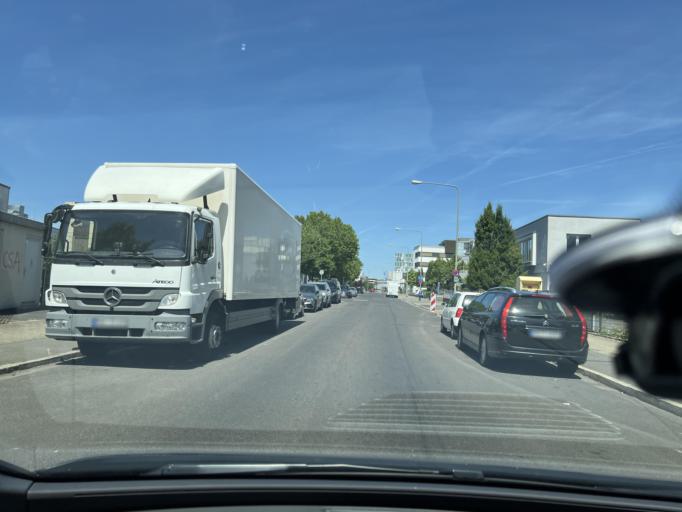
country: DE
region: Hesse
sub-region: Regierungsbezirk Darmstadt
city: Offenbach
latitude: 50.1202
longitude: 8.7599
